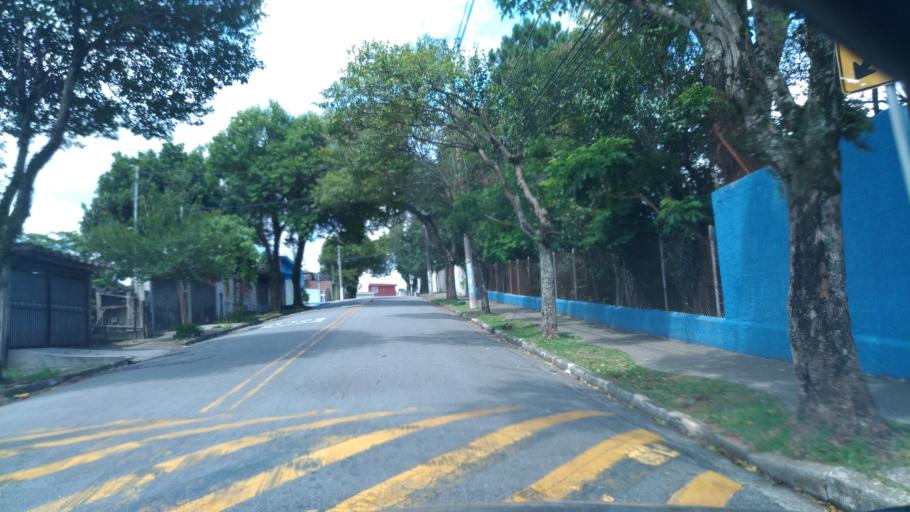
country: BR
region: Sao Paulo
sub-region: Sao Bernardo Do Campo
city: Sao Bernardo do Campo
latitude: -23.7063
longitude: -46.5858
